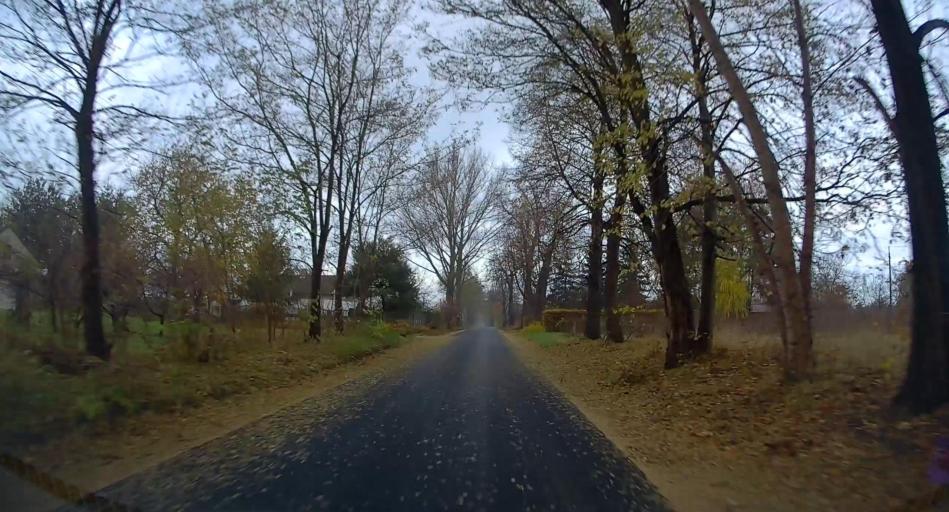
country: PL
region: Lodz Voivodeship
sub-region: Powiat skierniewicki
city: Kowiesy
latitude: 51.9238
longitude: 20.4096
